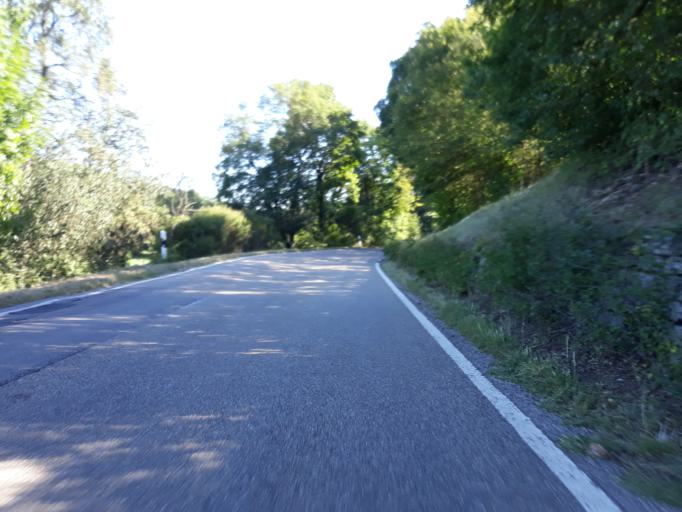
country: DE
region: Baden-Wuerttemberg
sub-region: Regierungsbezirk Stuttgart
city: Aidlingen
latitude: 48.6910
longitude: 8.8994
